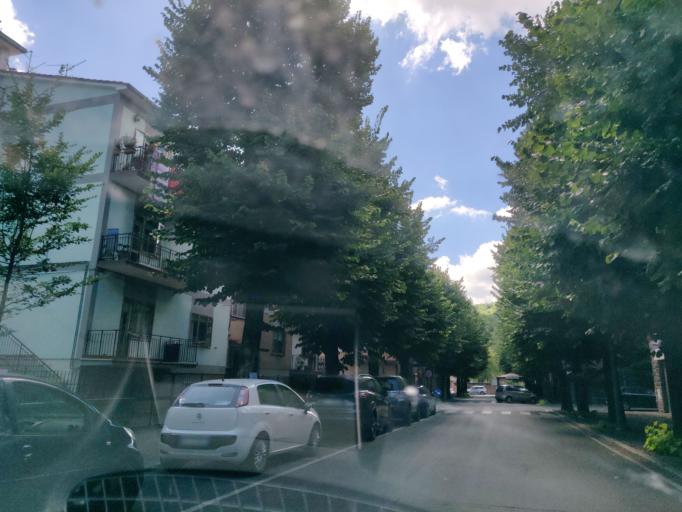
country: IT
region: Tuscany
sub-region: Provincia di Siena
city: Abbadia San Salvatore
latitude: 42.8804
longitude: 11.6710
